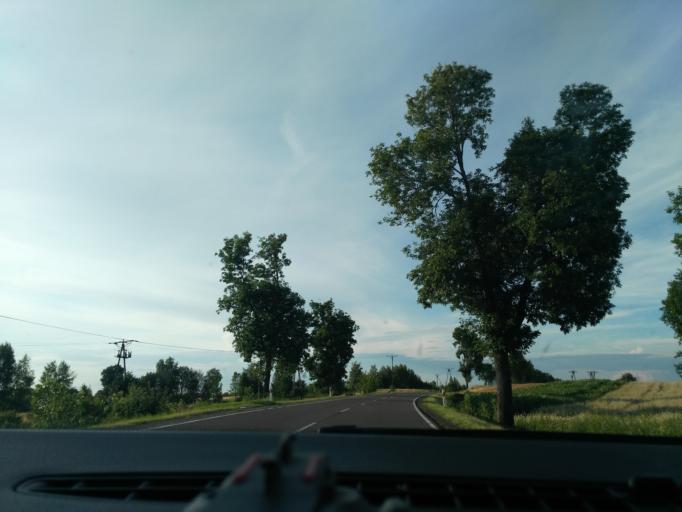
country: PL
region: Lublin Voivodeship
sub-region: Powiat krasnicki
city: Krasnik
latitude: 50.8839
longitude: 22.2607
